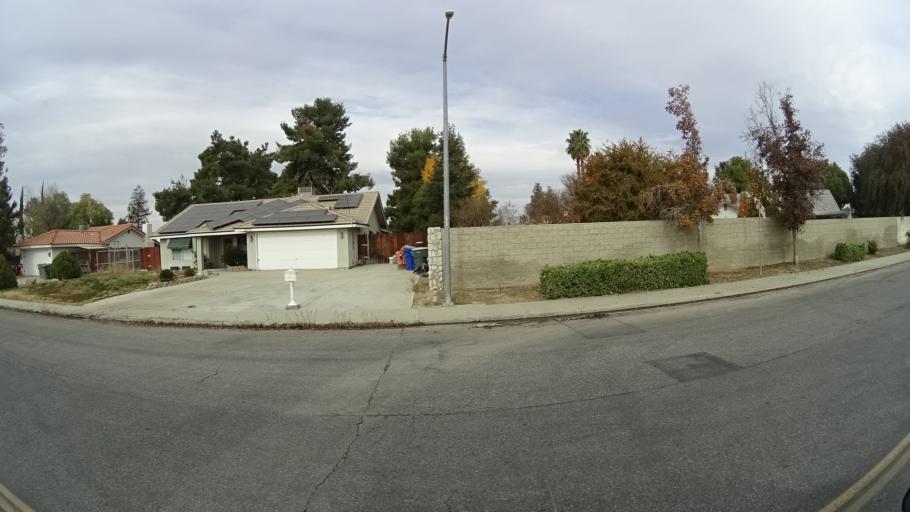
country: US
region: California
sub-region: Kern County
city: Greenacres
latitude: 35.3907
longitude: -119.1144
